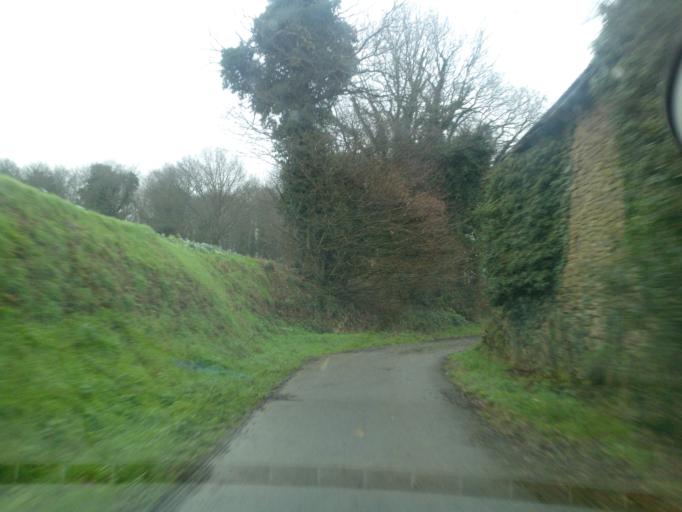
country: FR
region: Brittany
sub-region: Departement du Morbihan
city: Meneac
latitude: 48.1308
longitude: -2.4680
